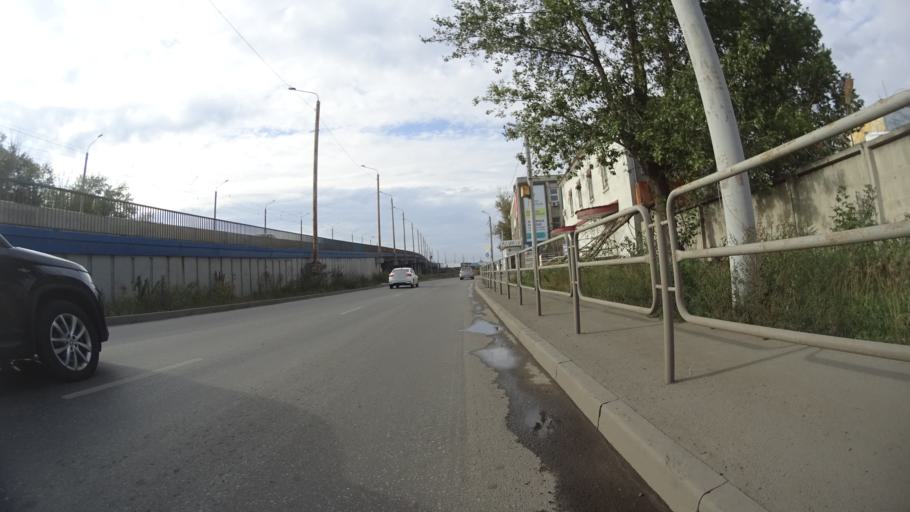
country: RU
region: Chelyabinsk
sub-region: Gorod Chelyabinsk
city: Chelyabinsk
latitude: 55.1952
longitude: 61.3888
